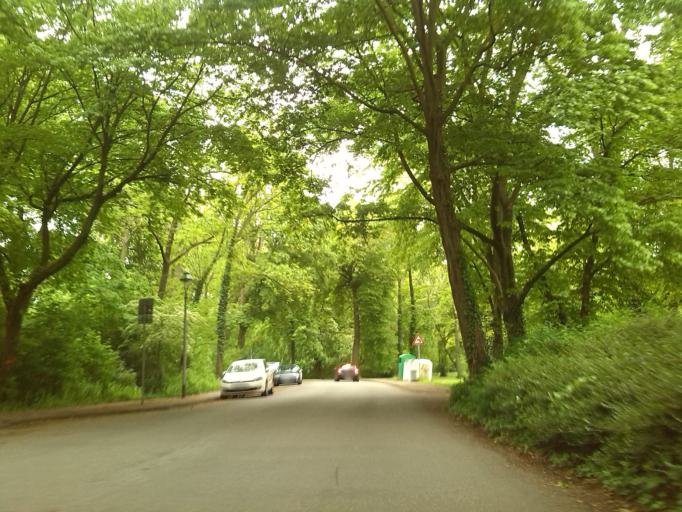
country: DE
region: Rheinland-Pfalz
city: Ludwigshafen am Rhein
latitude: 49.4704
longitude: 8.4661
